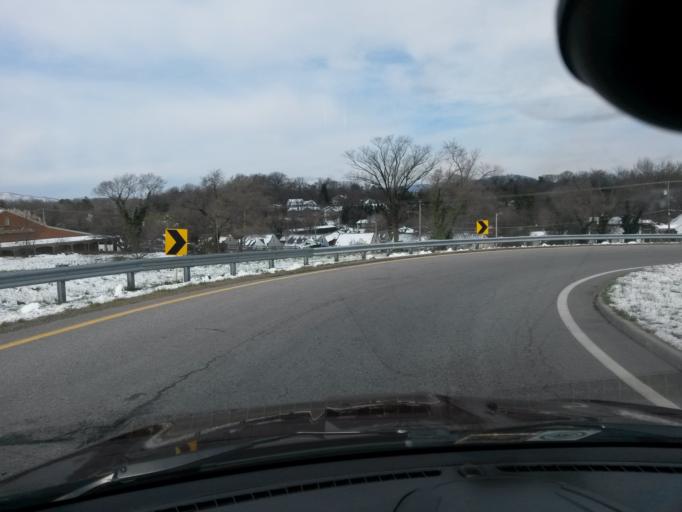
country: US
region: Virginia
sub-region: City of Roanoke
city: Roanoke
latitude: 37.2519
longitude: -79.9590
